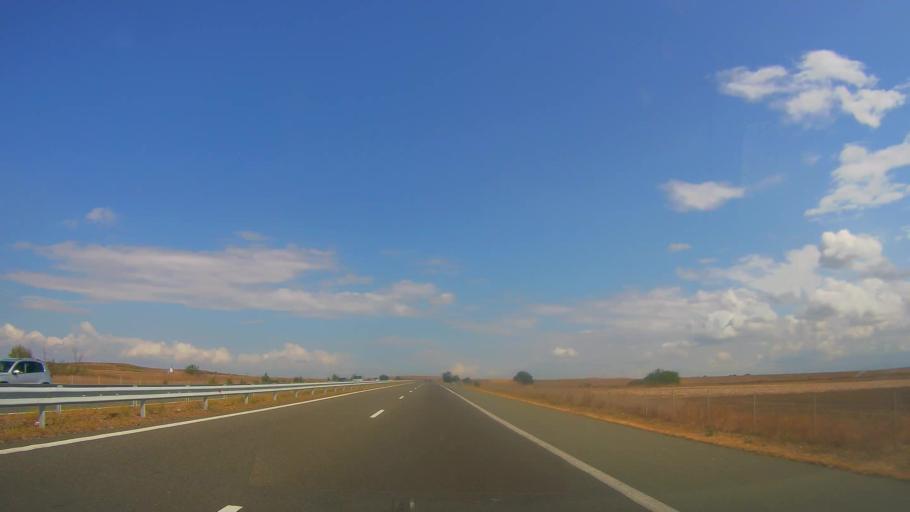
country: BG
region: Yambol
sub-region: Obshtina Straldzha
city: Straldzha
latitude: 42.5608
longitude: 26.8342
